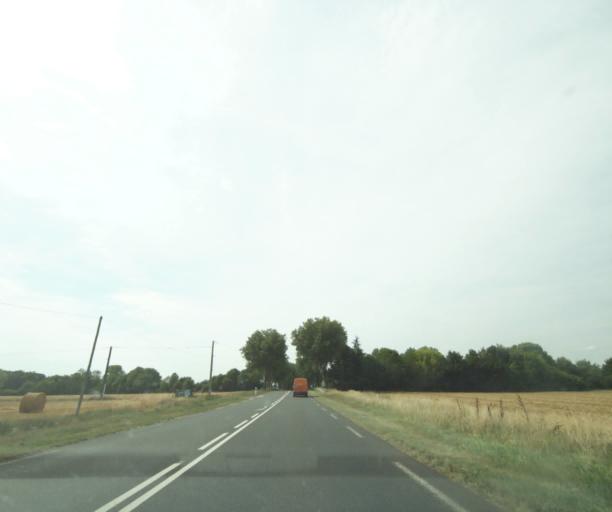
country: FR
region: Centre
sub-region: Departement d'Indre-et-Loire
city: Neuille-Pont-Pierre
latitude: 47.5232
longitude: 0.5785
